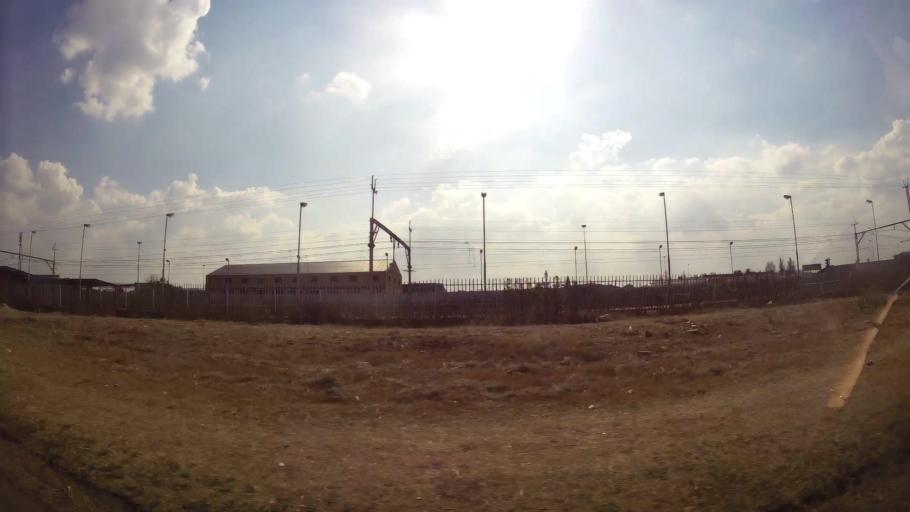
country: ZA
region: Gauteng
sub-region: Ekurhuleni Metropolitan Municipality
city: Germiston
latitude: -26.3260
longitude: 28.1594
